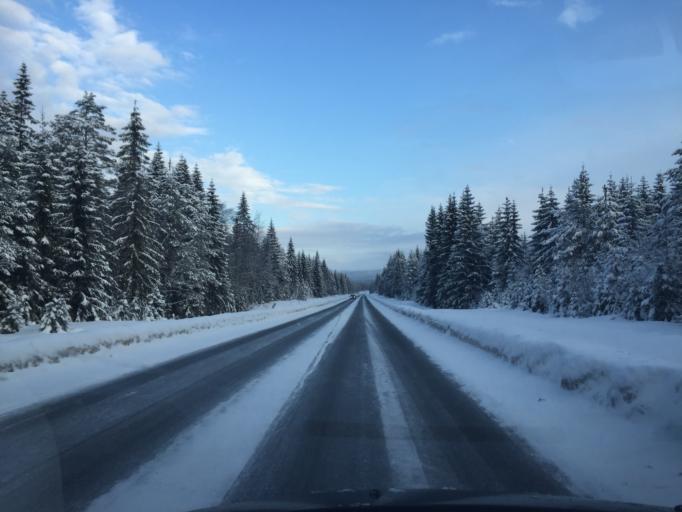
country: NO
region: Hedmark
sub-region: Trysil
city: Innbygda
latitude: 61.0741
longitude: 11.9742
